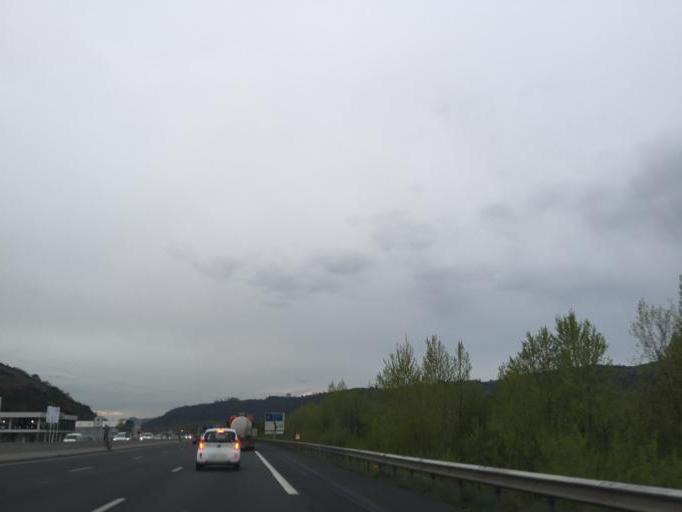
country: FR
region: Rhone-Alpes
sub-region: Departement de l'Isere
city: Seyssuel
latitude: 45.5517
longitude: 4.8296
